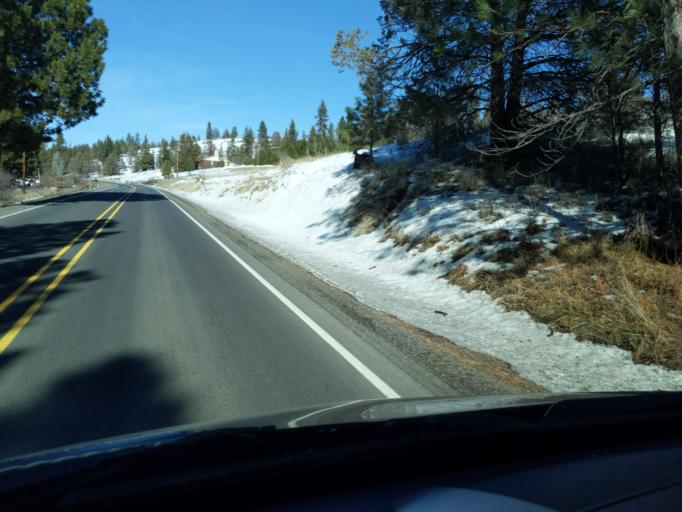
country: US
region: Oregon
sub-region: Grant County
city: John Day
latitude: 44.8783
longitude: -119.0156
